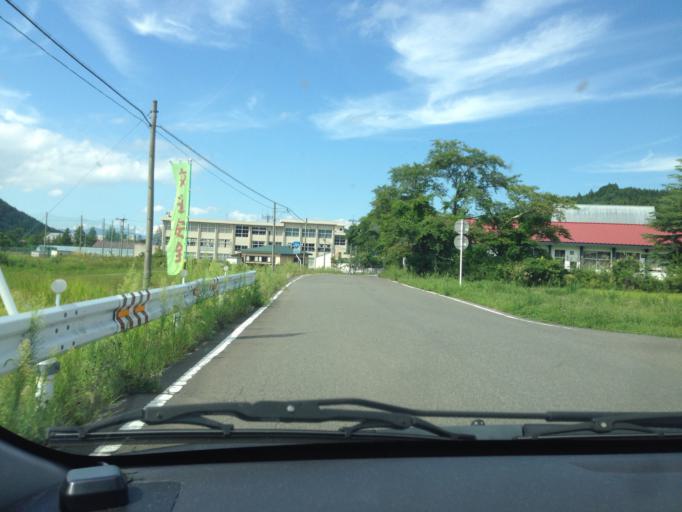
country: JP
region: Fukushima
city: Inawashiro
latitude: 37.3872
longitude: 140.0870
